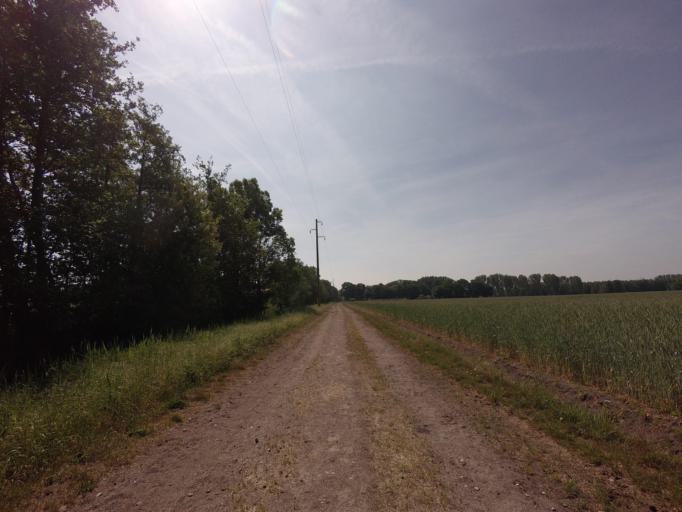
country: DE
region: Lower Saxony
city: Adenbuettel
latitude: 52.3758
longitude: 10.4336
